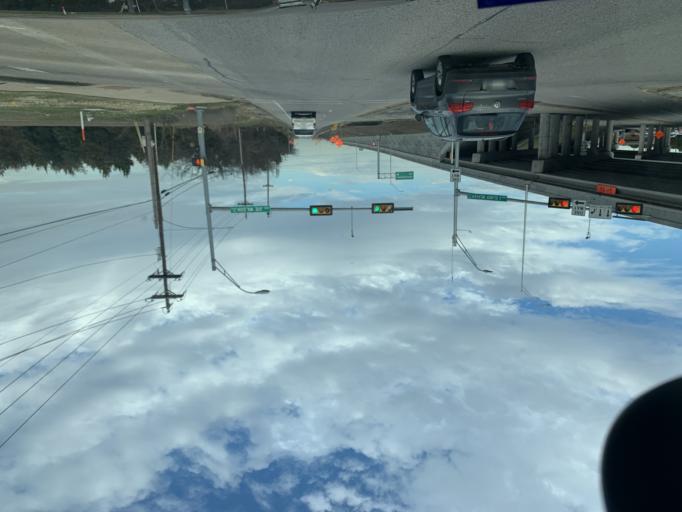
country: US
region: Texas
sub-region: Dallas County
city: Cedar Hill
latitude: 32.6094
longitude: -96.9254
